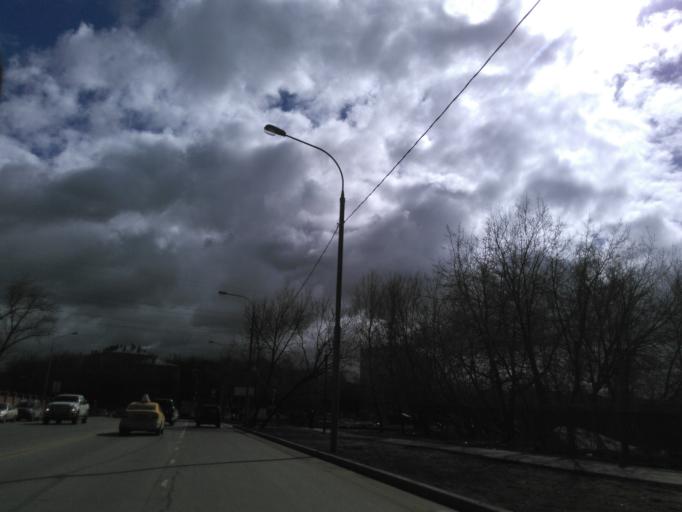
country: RU
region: Moscow
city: Golovinskiy
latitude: 55.8375
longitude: 37.5029
